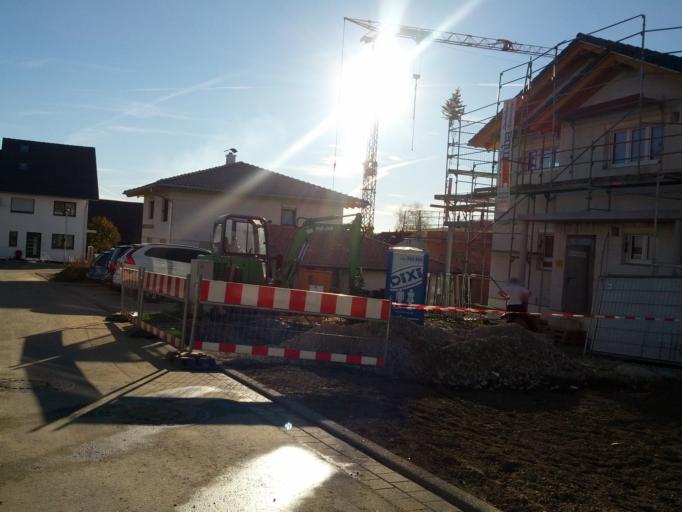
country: DE
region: Baden-Wuerttemberg
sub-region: Freiburg Region
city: Pfaffenweiler
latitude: 47.9421
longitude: 7.7574
